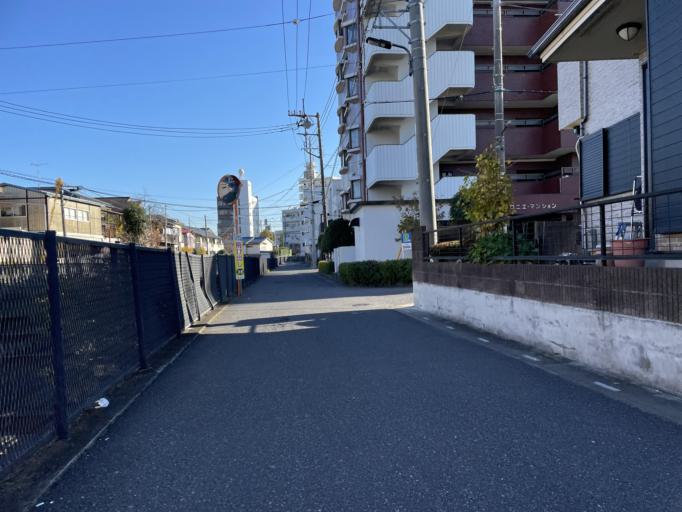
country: JP
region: Saitama
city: Soka
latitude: 35.8292
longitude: 139.8123
